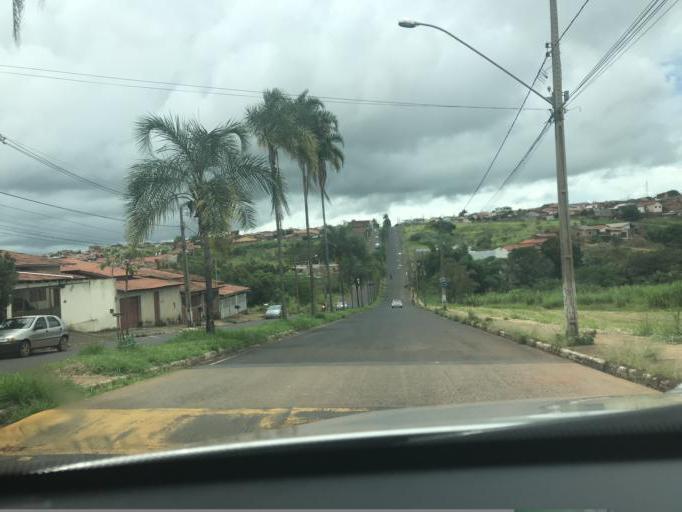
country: BR
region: Minas Gerais
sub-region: Araxa
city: Araxa
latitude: -19.5786
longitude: -46.9330
